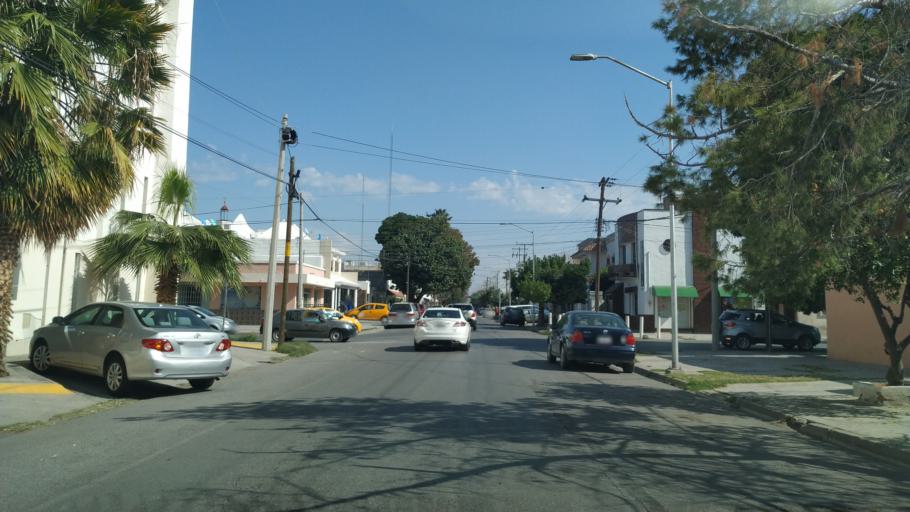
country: MX
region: Coahuila
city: Torreon
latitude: 25.5451
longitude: -103.4509
